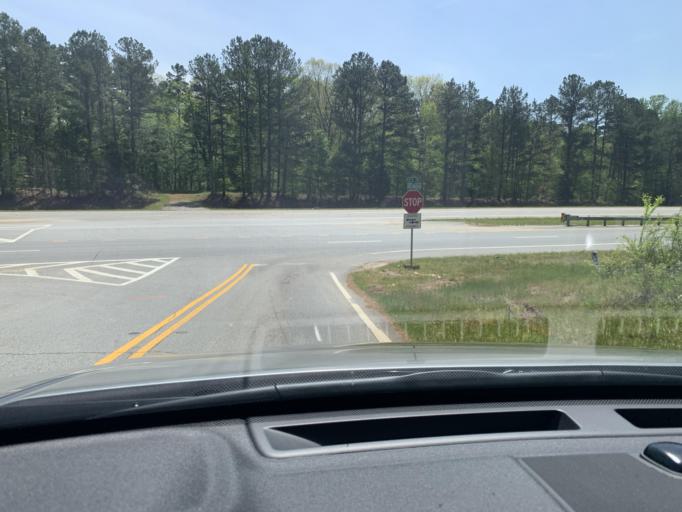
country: US
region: Georgia
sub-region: Barrow County
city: Statham
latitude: 33.8839
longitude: -83.5908
